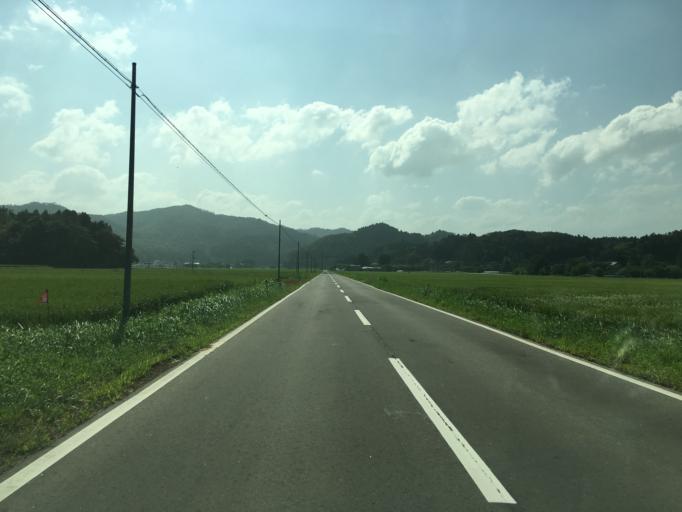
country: JP
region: Miyagi
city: Marumori
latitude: 37.8932
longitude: 140.8225
